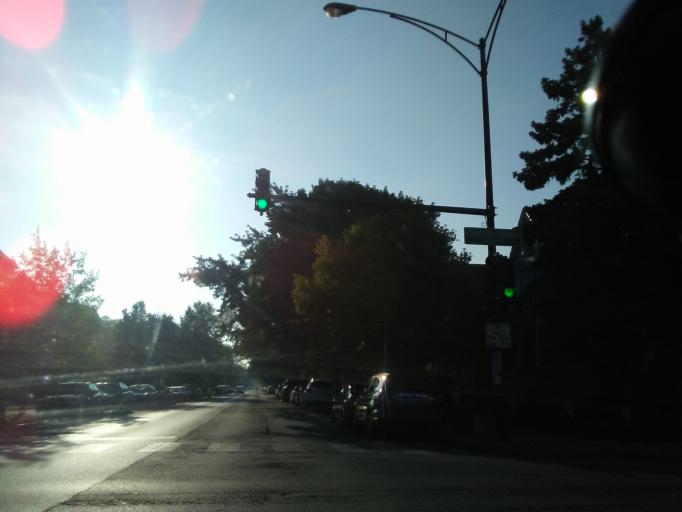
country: US
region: Illinois
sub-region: Cook County
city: Lincolnwood
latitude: 41.9282
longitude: -87.7171
